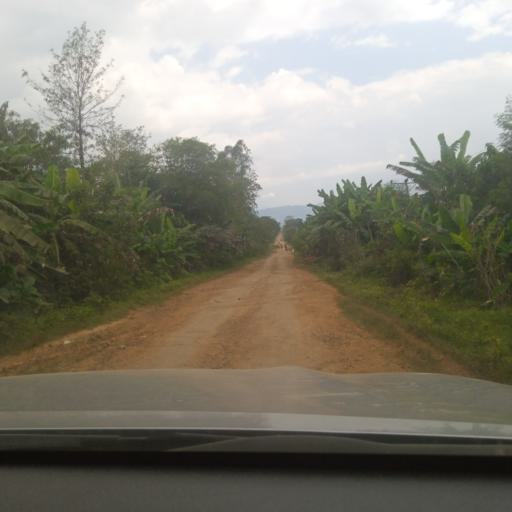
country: ET
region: Southern Nations, Nationalities, and People's Region
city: Tippi
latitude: 7.1386
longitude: 35.4211
